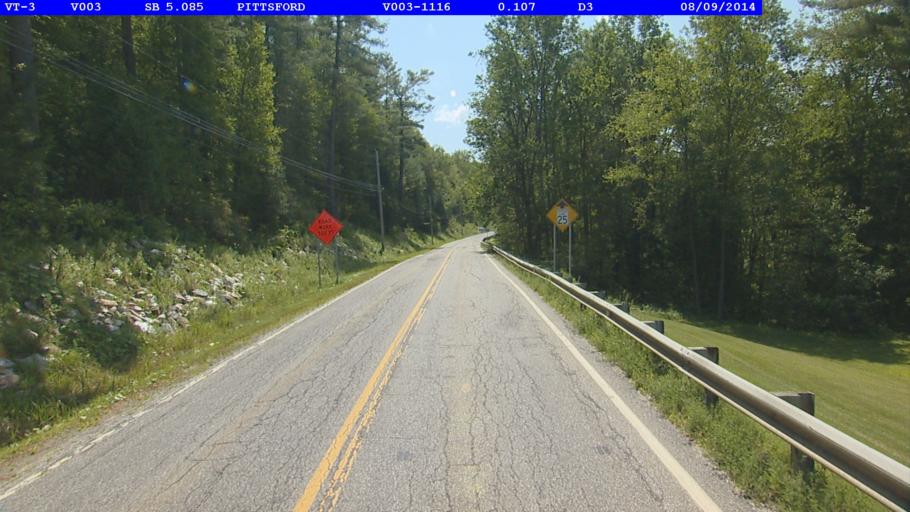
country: US
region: Vermont
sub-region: Rutland County
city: Rutland
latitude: 43.6678
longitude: -73.0226
